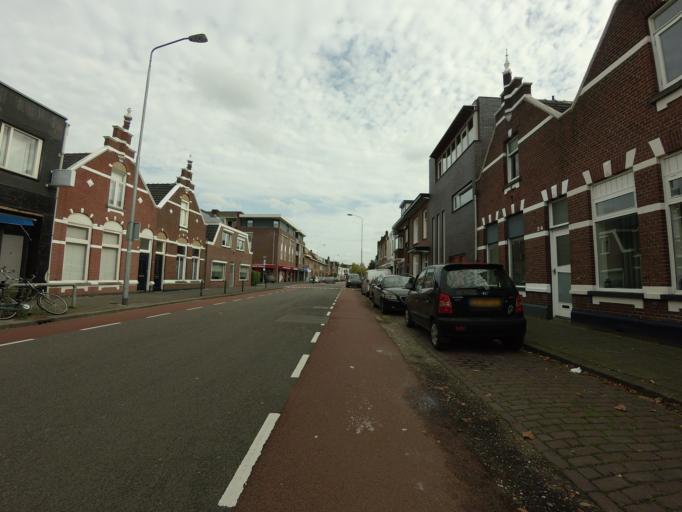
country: NL
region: North Brabant
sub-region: Gemeente Breda
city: Breda
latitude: 51.5804
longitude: 4.7860
